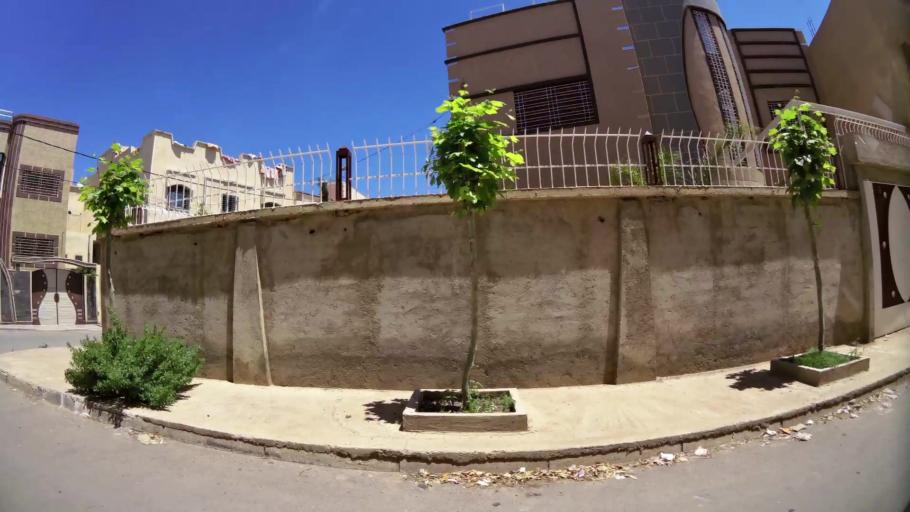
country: MA
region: Oriental
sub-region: Oujda-Angad
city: Oujda
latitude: 34.6639
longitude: -1.9212
